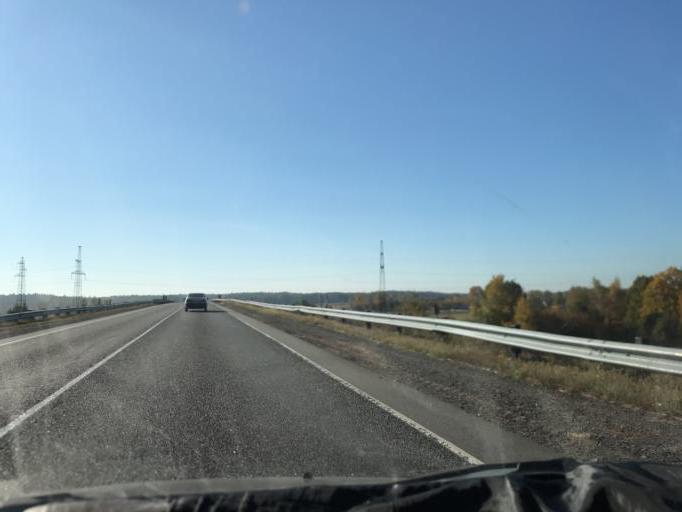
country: BY
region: Mogilev
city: Babruysk
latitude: 53.1825
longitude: 29.0479
